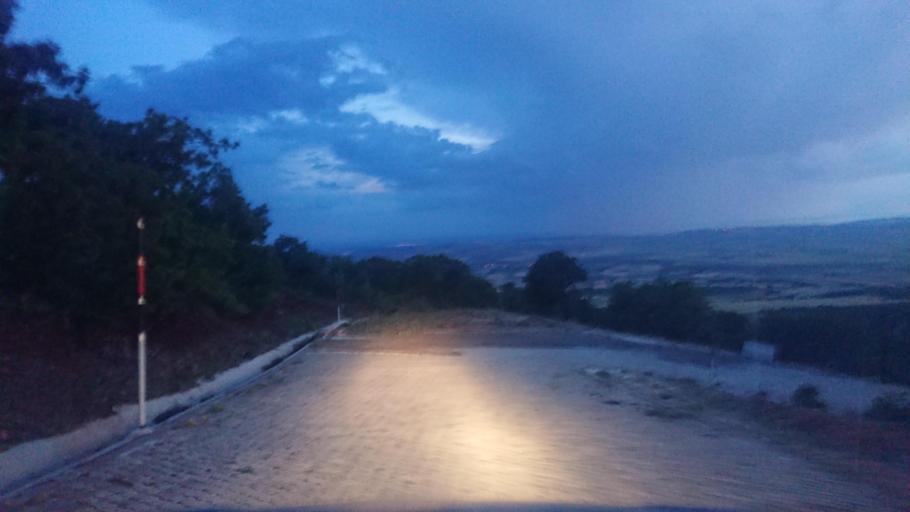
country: TR
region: Aksaray
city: Ortakoy
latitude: 38.6432
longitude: 34.0240
